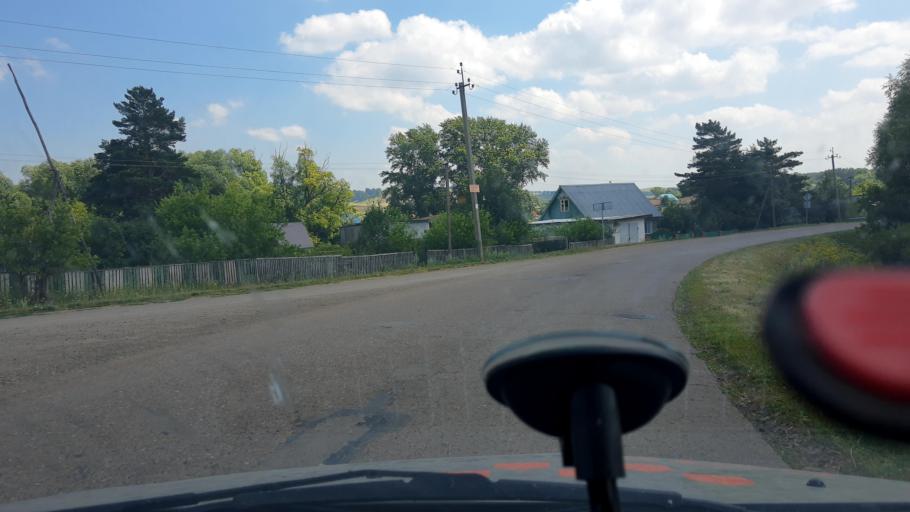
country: RU
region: Bashkortostan
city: Chekmagush
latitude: 54.8826
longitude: 54.6047
